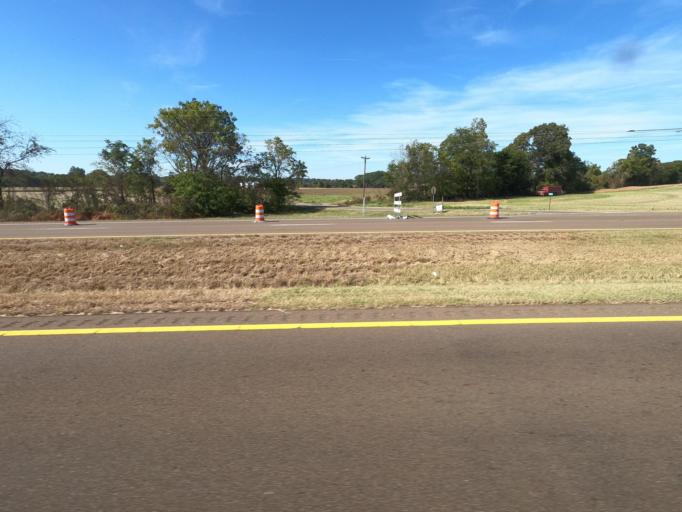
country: US
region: Tennessee
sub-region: Obion County
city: Englewood
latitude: 36.3683
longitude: -89.1250
